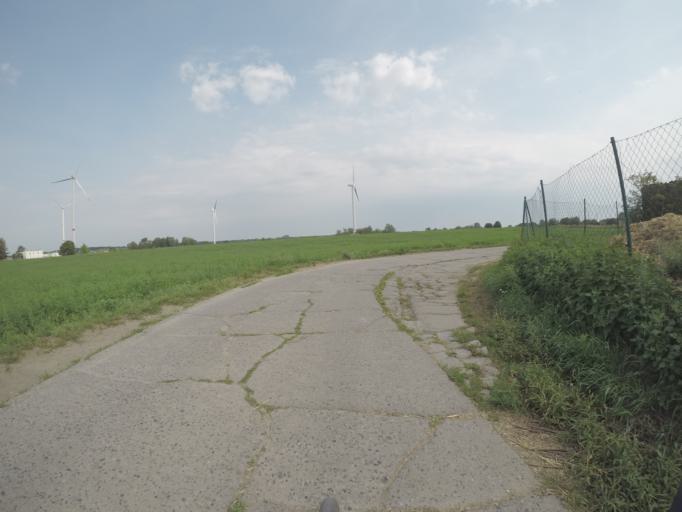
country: DE
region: Berlin
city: Blankenfelde
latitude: 52.6615
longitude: 13.4240
